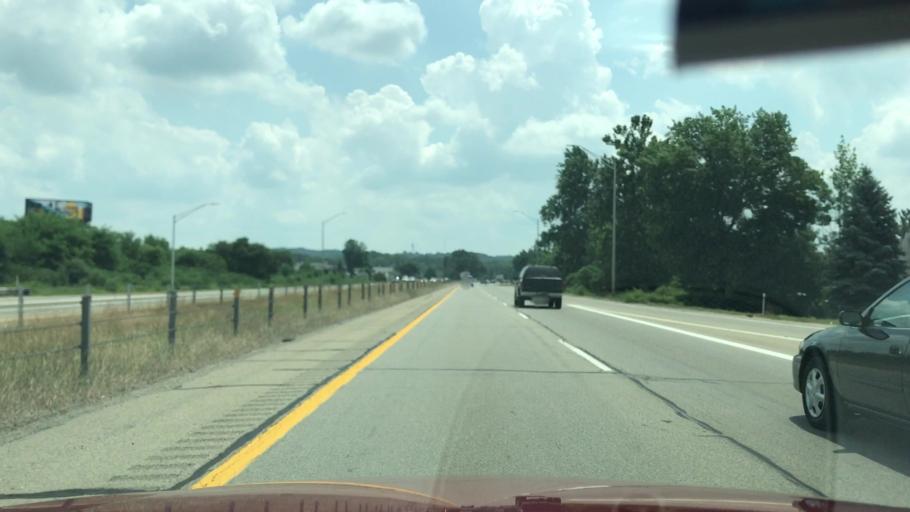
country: US
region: Michigan
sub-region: Kent County
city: Cutlerville
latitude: 42.8252
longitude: -85.6715
